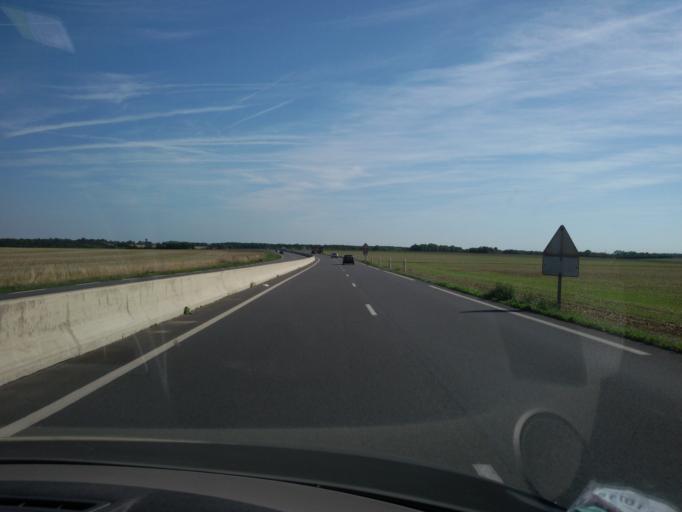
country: FR
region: Ile-de-France
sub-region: Departement de l'Essonne
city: Mereville
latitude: 48.3549
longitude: 2.0546
